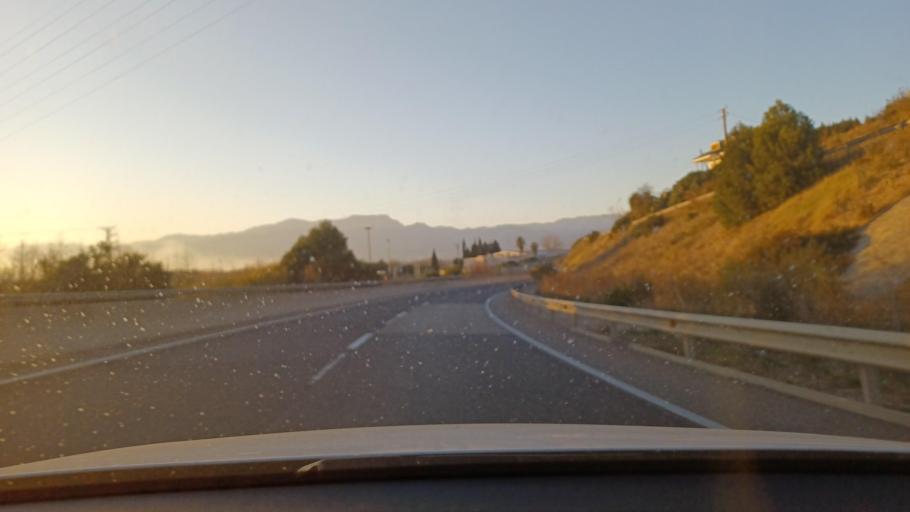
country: ES
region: Catalonia
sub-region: Provincia de Tarragona
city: Tortosa
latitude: 40.7718
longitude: 0.5412
